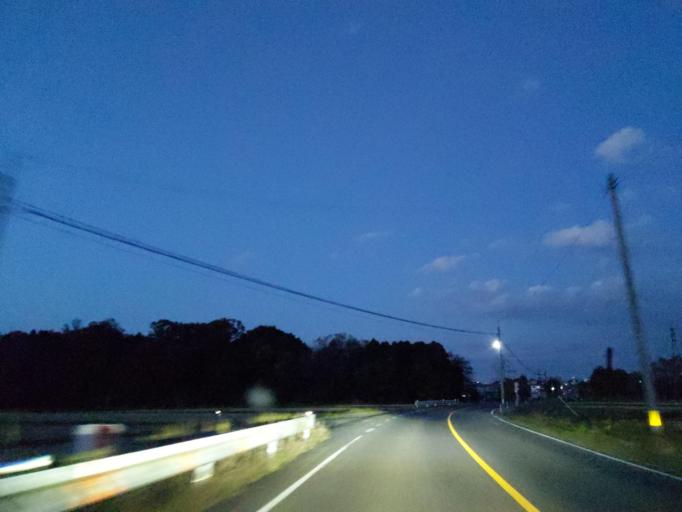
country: JP
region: Fukushima
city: Koriyama
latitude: 37.4282
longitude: 140.3262
